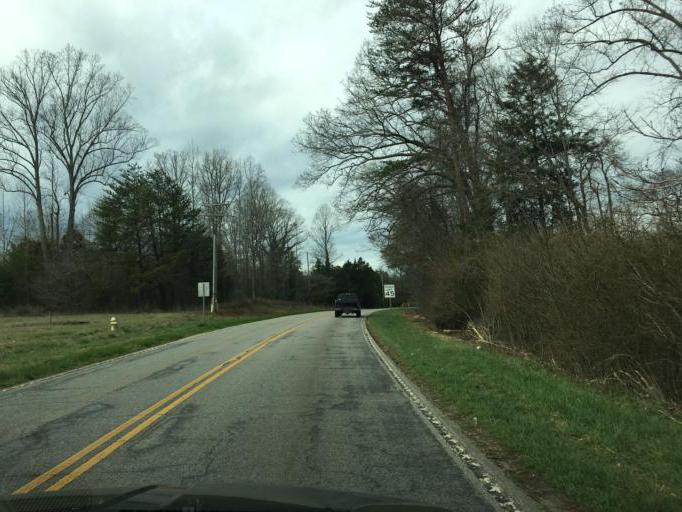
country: US
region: South Carolina
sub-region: Anderson County
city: Piedmont
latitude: 34.7004
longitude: -82.4292
